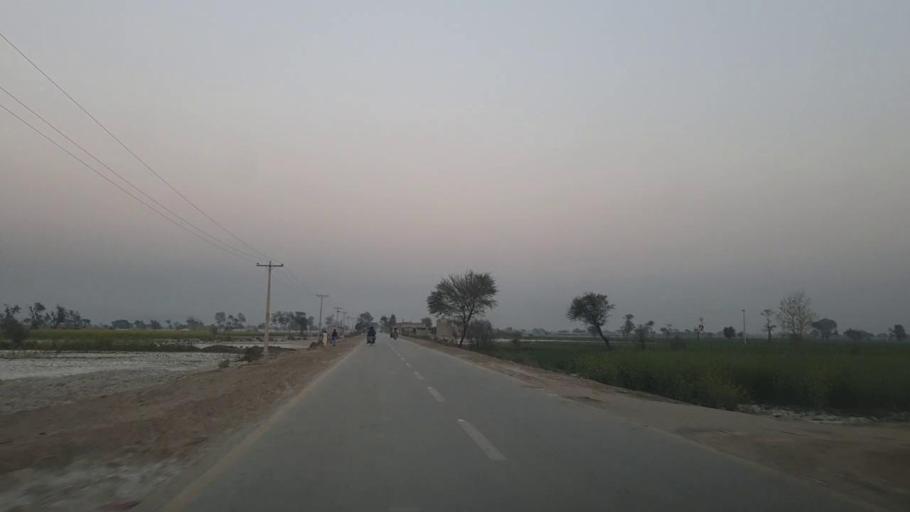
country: PK
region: Sindh
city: Naushahro Firoz
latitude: 26.8489
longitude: 68.0507
